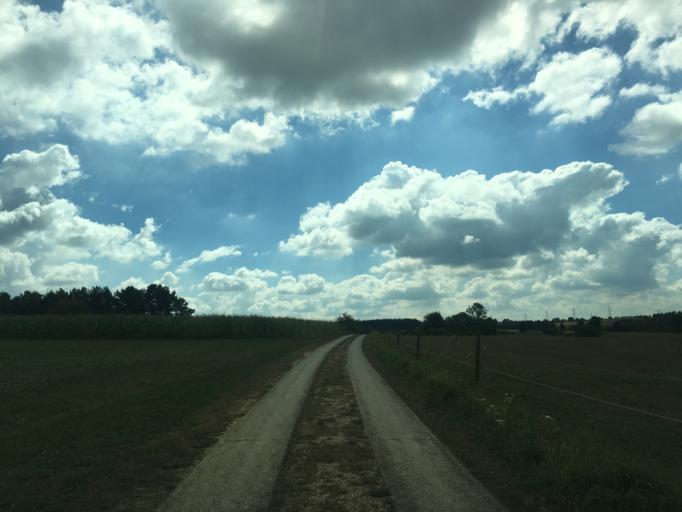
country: DE
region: Baden-Wuerttemberg
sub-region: Tuebingen Region
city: Hayingen
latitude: 48.2740
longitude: 9.4912
